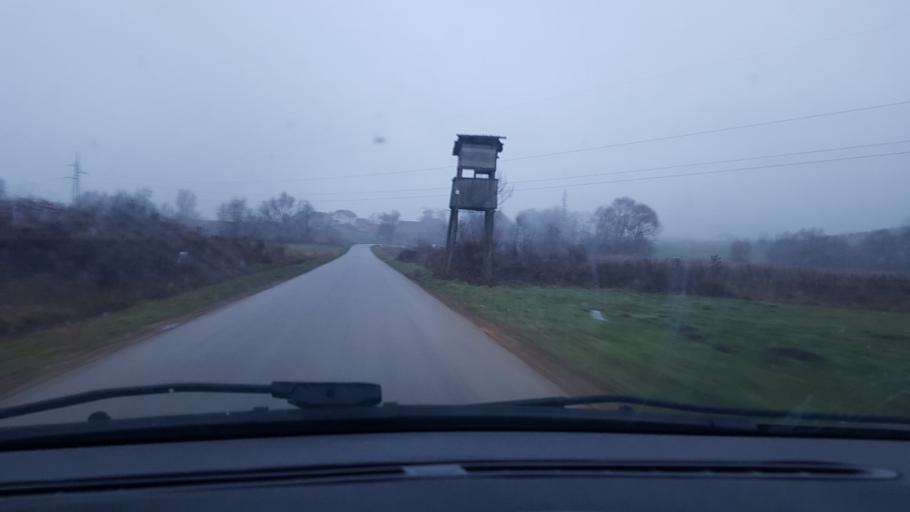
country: HR
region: Krapinsko-Zagorska
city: Zabok
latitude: 46.0400
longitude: 15.9219
